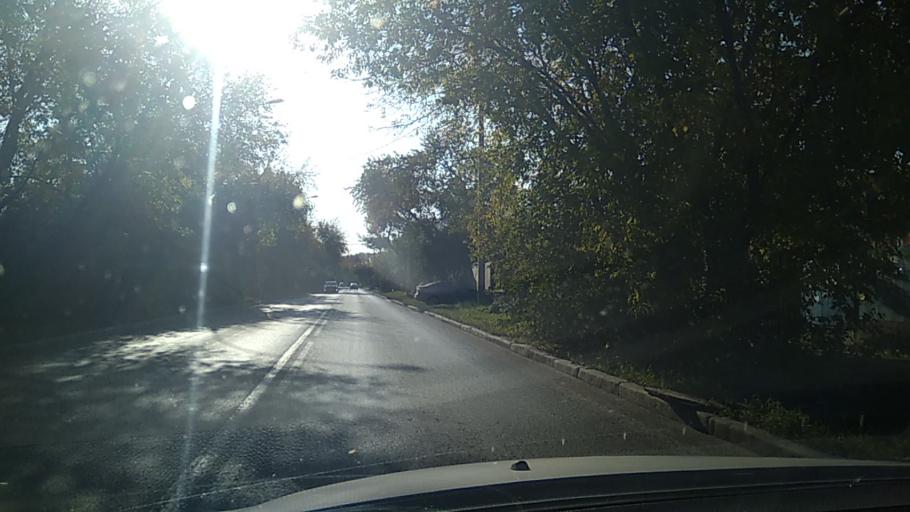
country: RU
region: Sverdlovsk
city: Yekaterinburg
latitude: 56.7801
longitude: 60.6477
